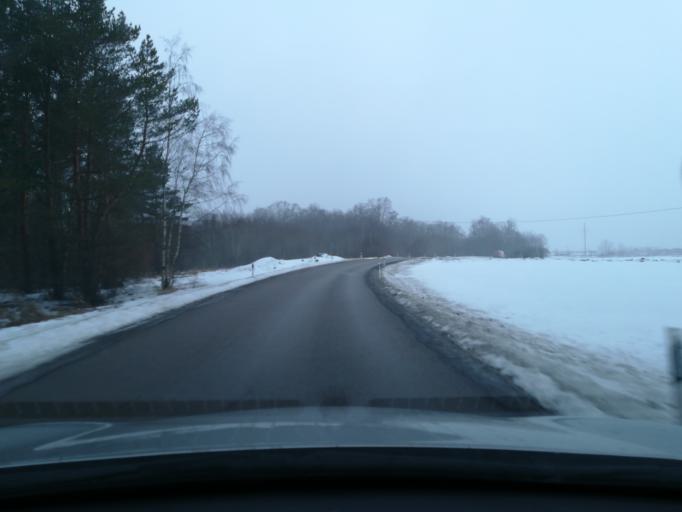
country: EE
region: Harju
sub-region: Rae vald
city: Jueri
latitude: 59.3761
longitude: 24.8982
